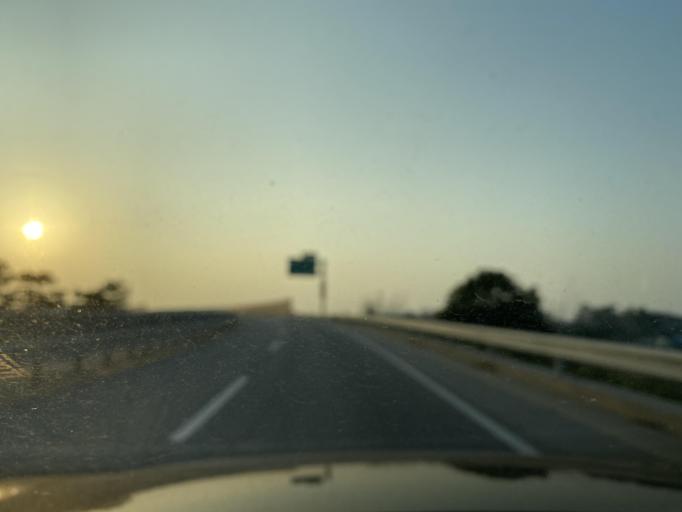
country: KR
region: Chungcheongnam-do
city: Yesan
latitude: 36.6968
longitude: 126.7985
